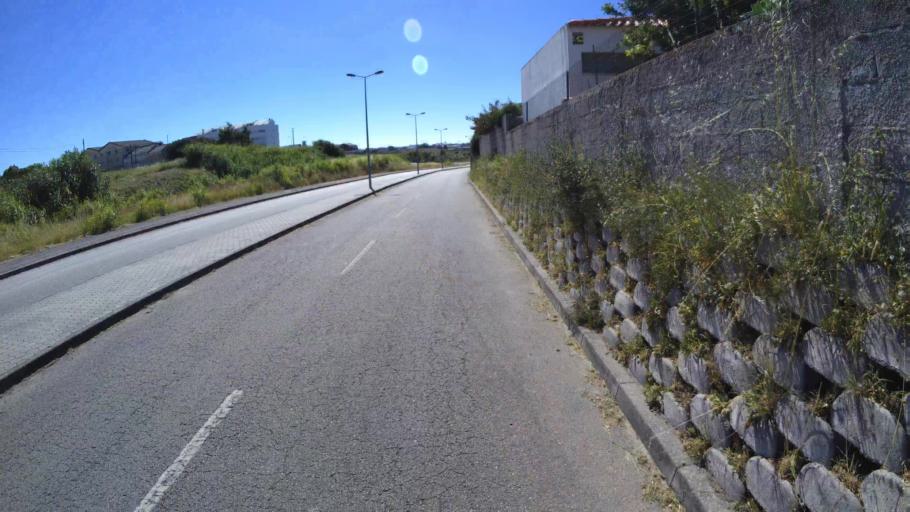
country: PT
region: Aveiro
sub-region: Aveiro
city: Aveiro
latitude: 40.6511
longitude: -8.6399
